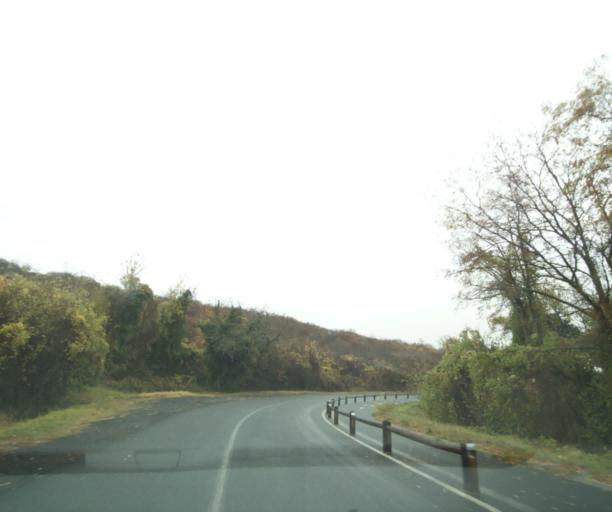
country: FR
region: Auvergne
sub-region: Departement du Puy-de-Dome
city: Cournon-d'Auvergne
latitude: 45.7571
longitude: 3.2065
